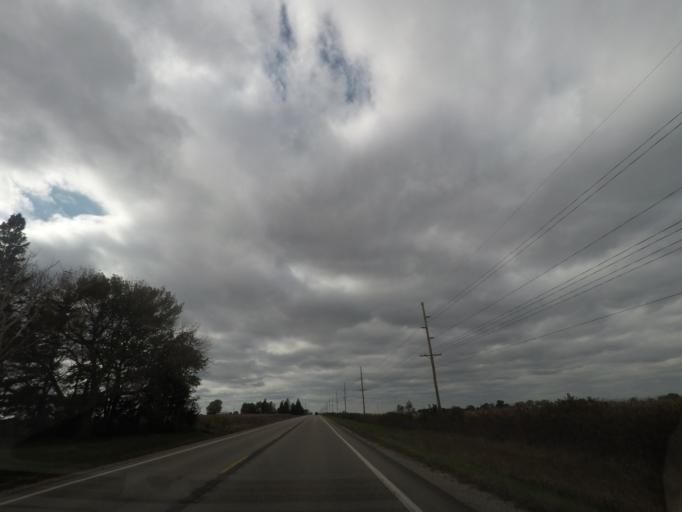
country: US
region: Iowa
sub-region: Story County
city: Huxley
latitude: 41.8778
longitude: -93.5502
